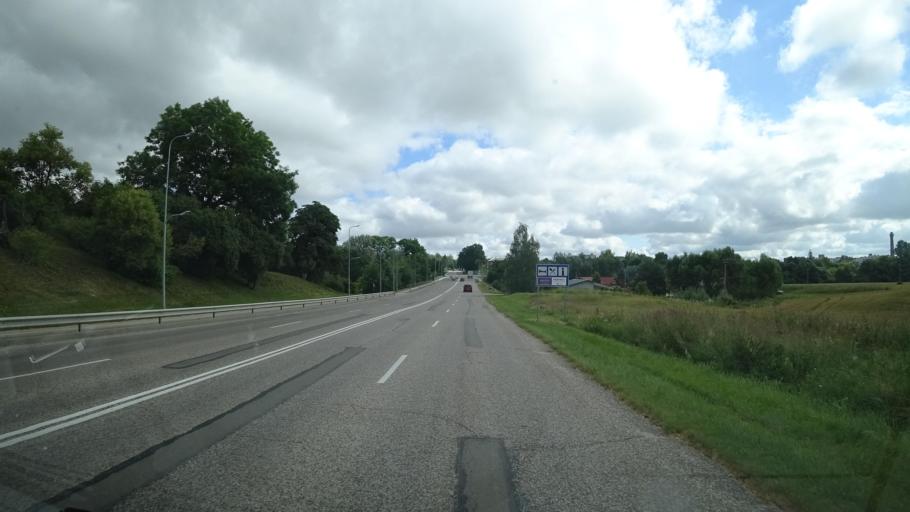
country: LT
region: Marijampoles apskritis
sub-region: Marijampole Municipality
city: Marijampole
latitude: 54.5353
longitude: 23.3369
